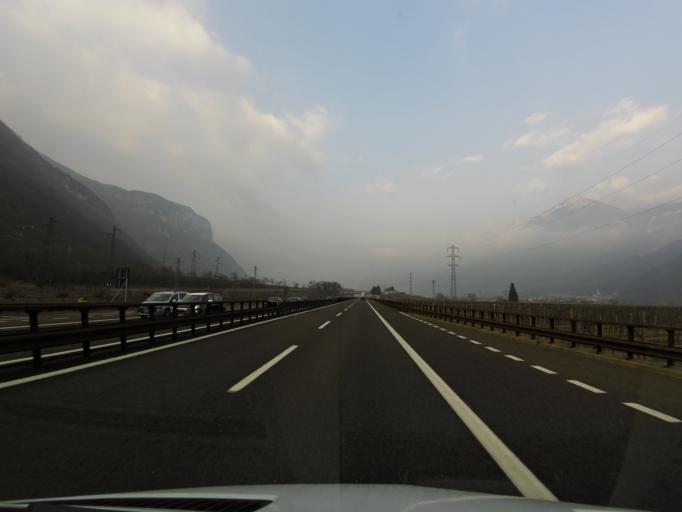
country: IT
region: Veneto
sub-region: Provincia di Verona
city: Rivalta
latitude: 45.6488
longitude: 10.8858
